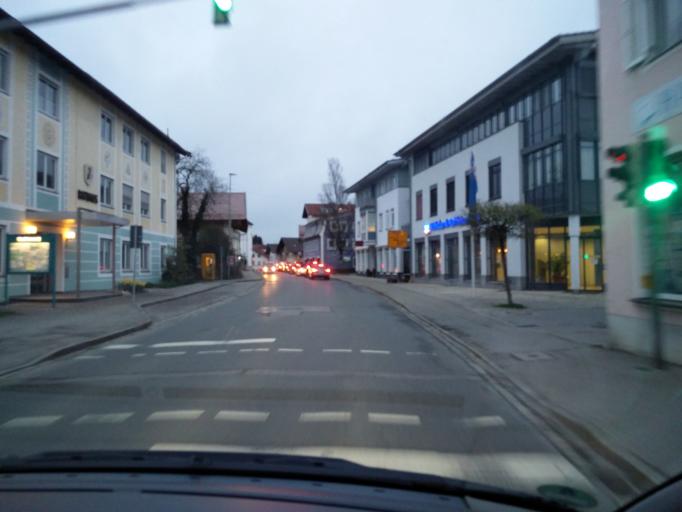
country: DE
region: Bavaria
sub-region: Upper Bavaria
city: Bad Endorf
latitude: 47.9077
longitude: 12.2993
